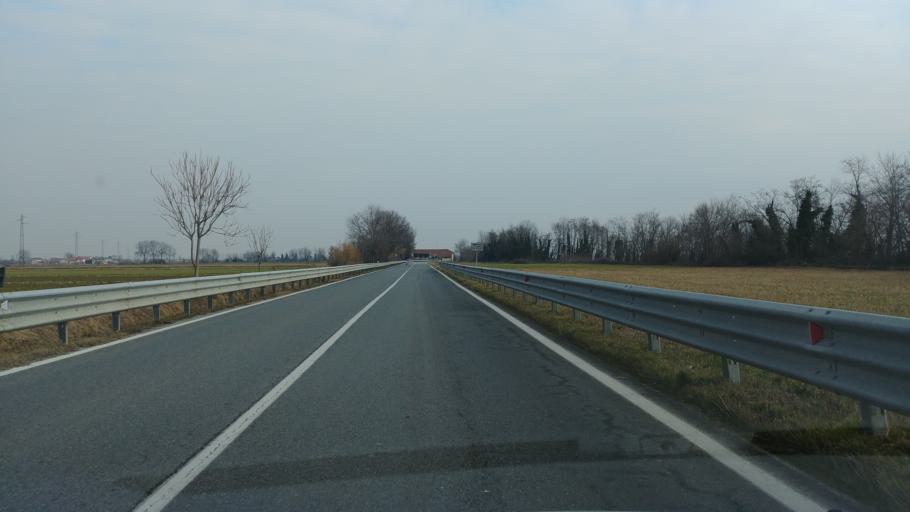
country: IT
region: Piedmont
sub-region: Provincia di Cuneo
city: Castelletto Stura
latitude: 44.4457
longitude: 7.6110
